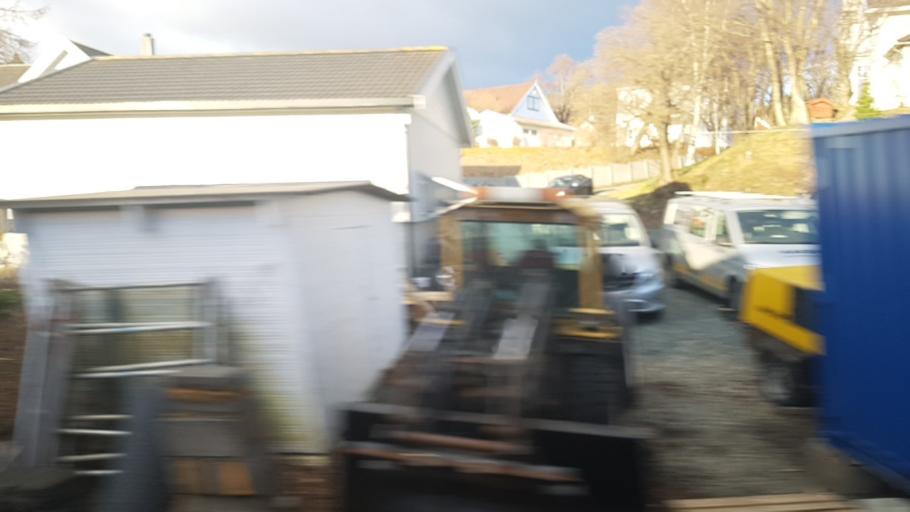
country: NO
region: Sor-Trondelag
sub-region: Klaebu
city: Klaebu
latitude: 63.4275
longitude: 10.5370
